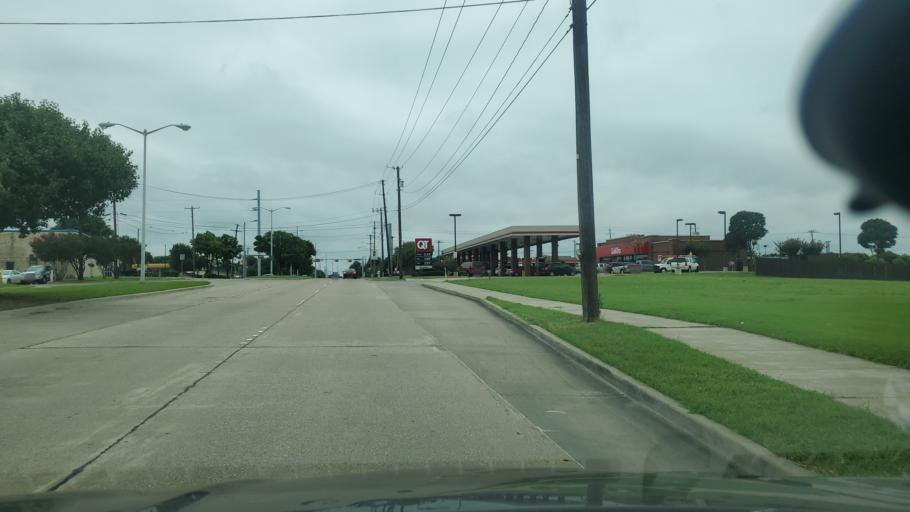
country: US
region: Texas
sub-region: Dallas County
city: Garland
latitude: 32.9464
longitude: -96.6654
